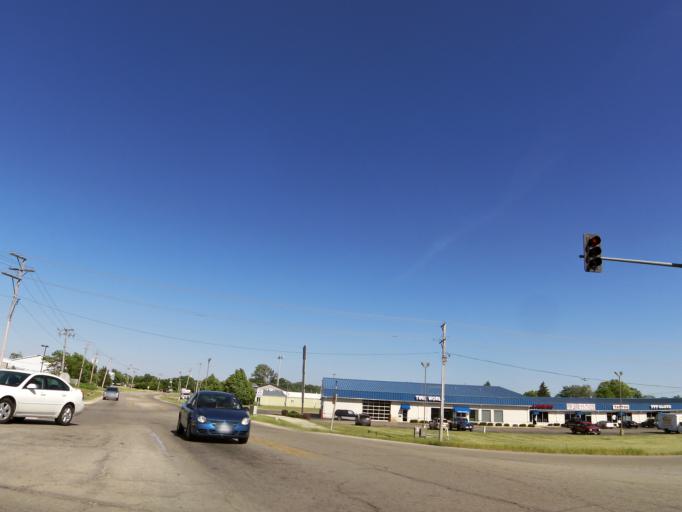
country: US
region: Illinois
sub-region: Winnebago County
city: Roscoe
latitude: 42.3919
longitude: -89.0160
